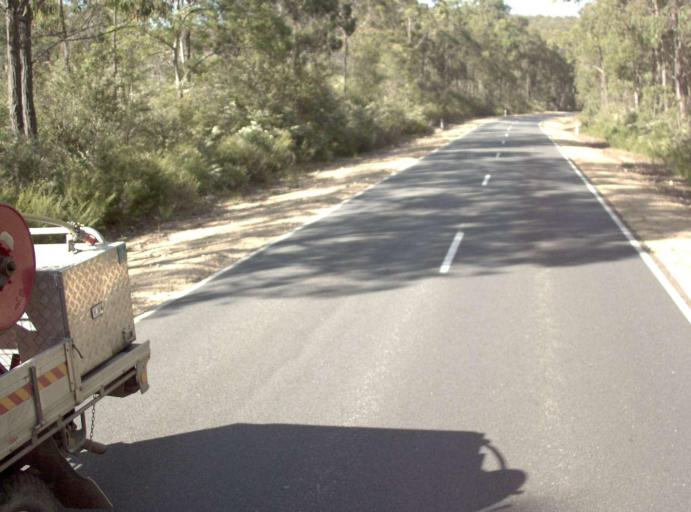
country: AU
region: Victoria
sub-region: East Gippsland
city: Lakes Entrance
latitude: -37.6492
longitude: 148.1046
